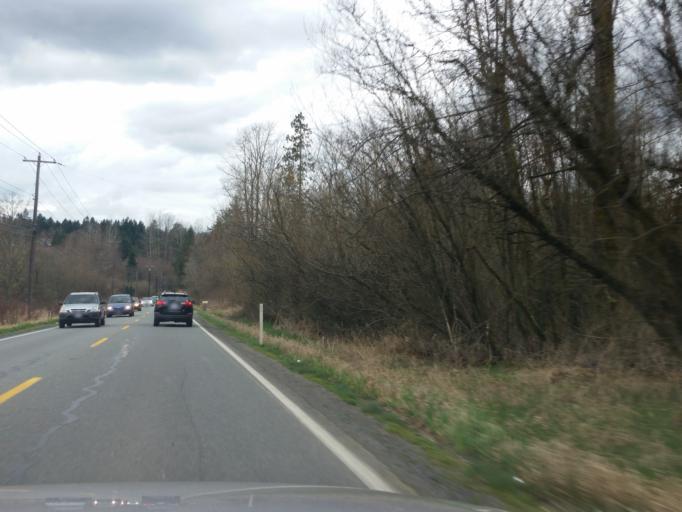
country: US
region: Washington
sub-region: Snohomish County
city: North Creek
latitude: 47.8050
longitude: -122.1541
